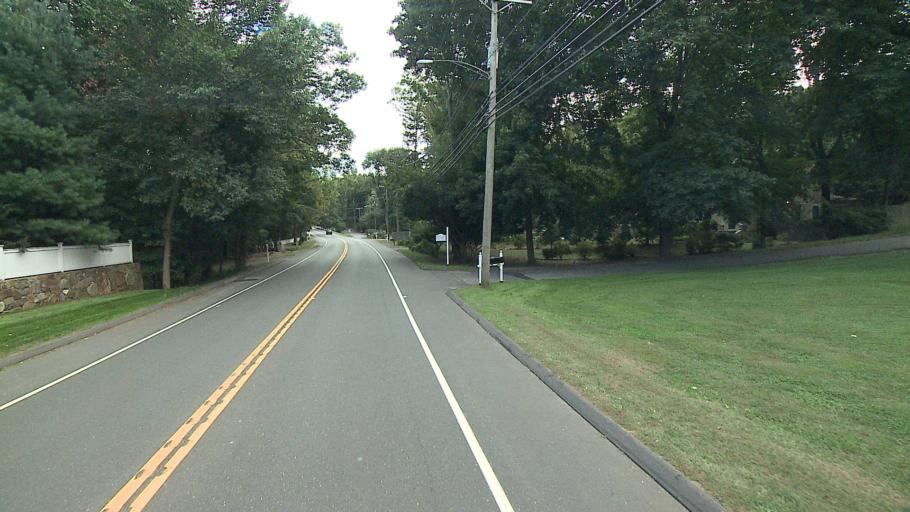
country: US
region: Connecticut
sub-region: Fairfield County
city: Westport
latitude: 41.1507
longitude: -73.3687
